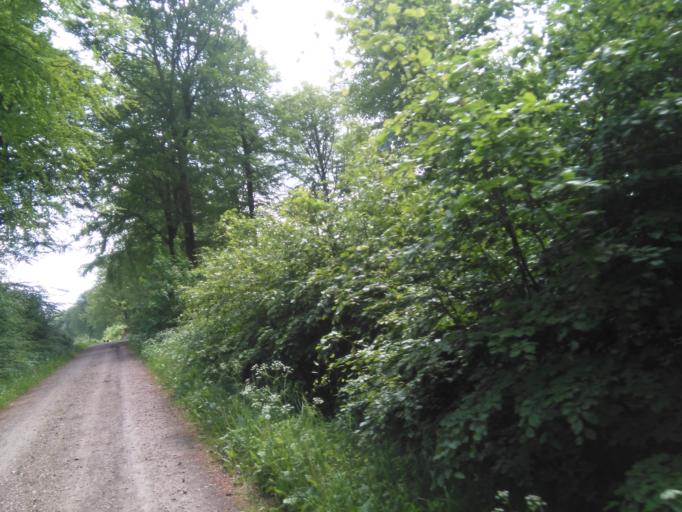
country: DK
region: Central Jutland
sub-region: Favrskov Kommune
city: Hinnerup
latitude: 56.2725
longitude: 10.0136
